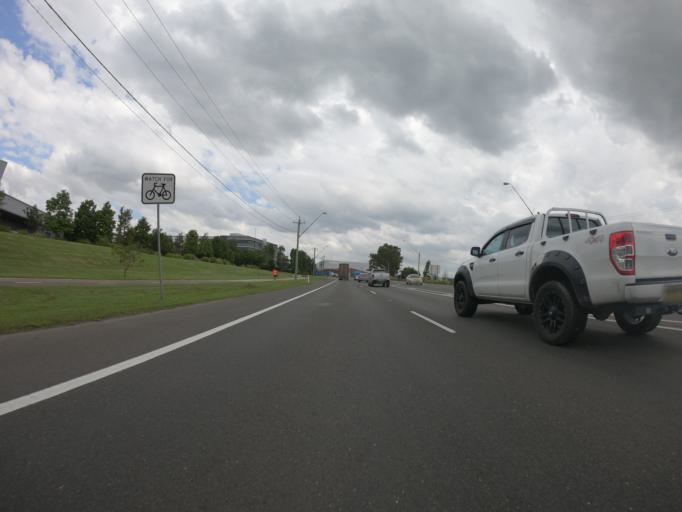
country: AU
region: New South Wales
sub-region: Blacktown
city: Mount Druitt
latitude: -33.8185
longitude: 150.7761
